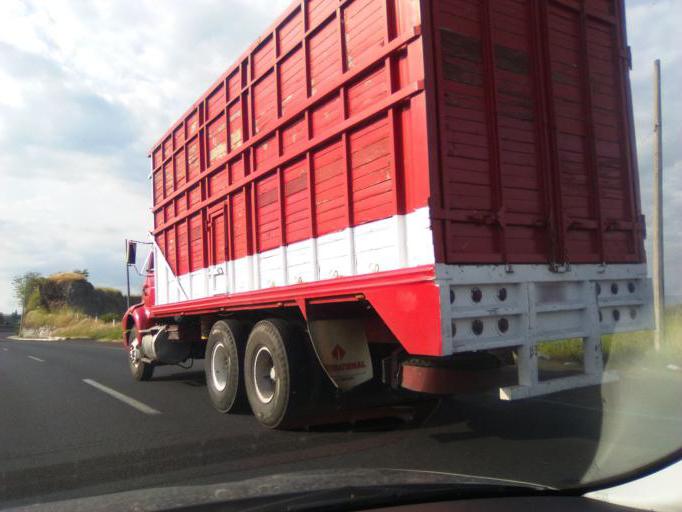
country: MX
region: Morelos
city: Temixco
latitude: 18.8662
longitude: -99.2224
